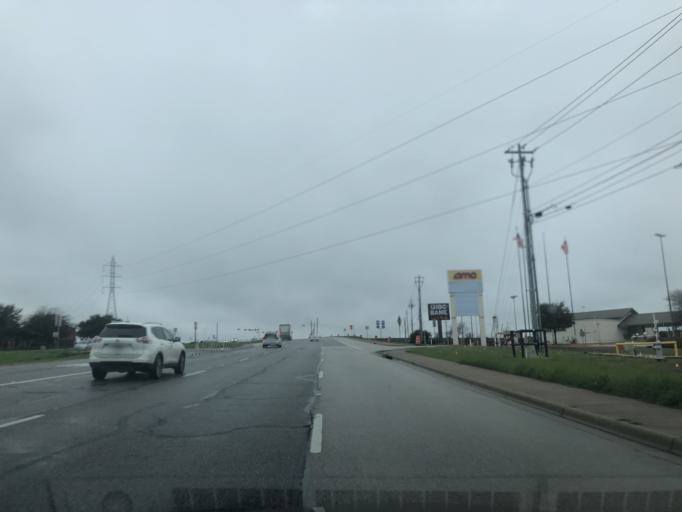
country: US
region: Texas
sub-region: Travis County
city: Wells Branch
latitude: 30.4067
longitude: -97.6708
